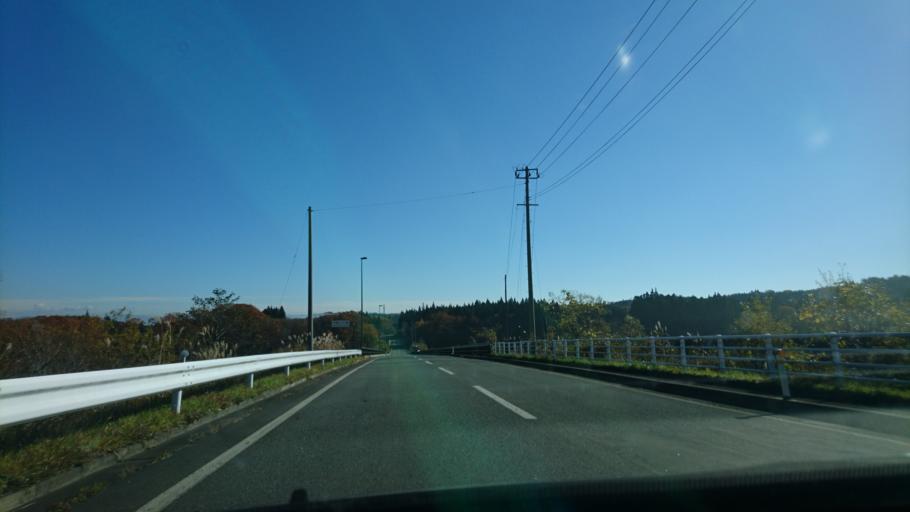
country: JP
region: Iwate
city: Mizusawa
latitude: 39.1201
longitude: 140.9467
